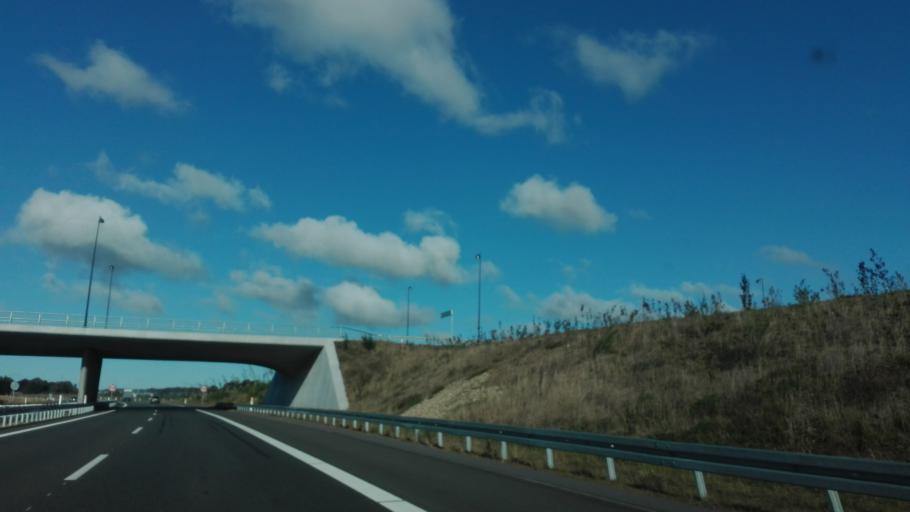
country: DK
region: Central Jutland
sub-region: Silkeborg Kommune
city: Silkeborg
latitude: 56.2006
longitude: 9.5518
